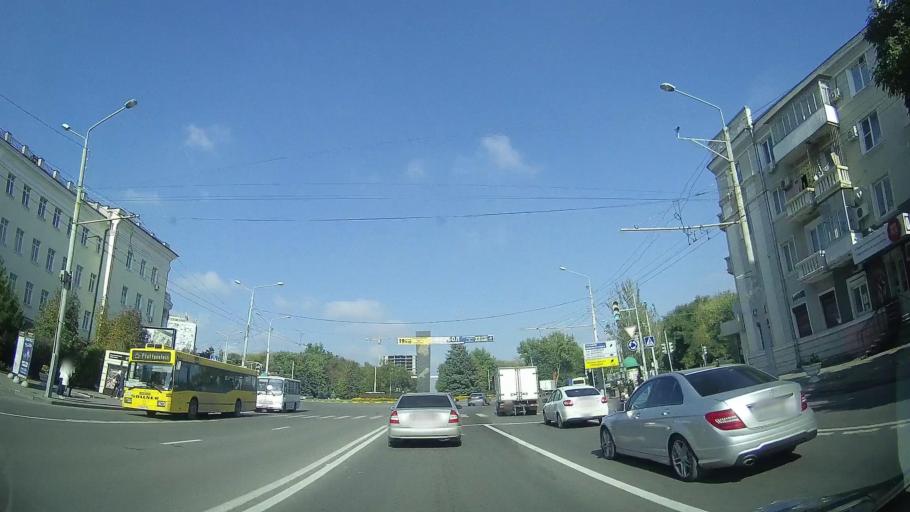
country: RU
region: Rostov
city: Rostov-na-Donu
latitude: 47.2370
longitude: 39.7000
